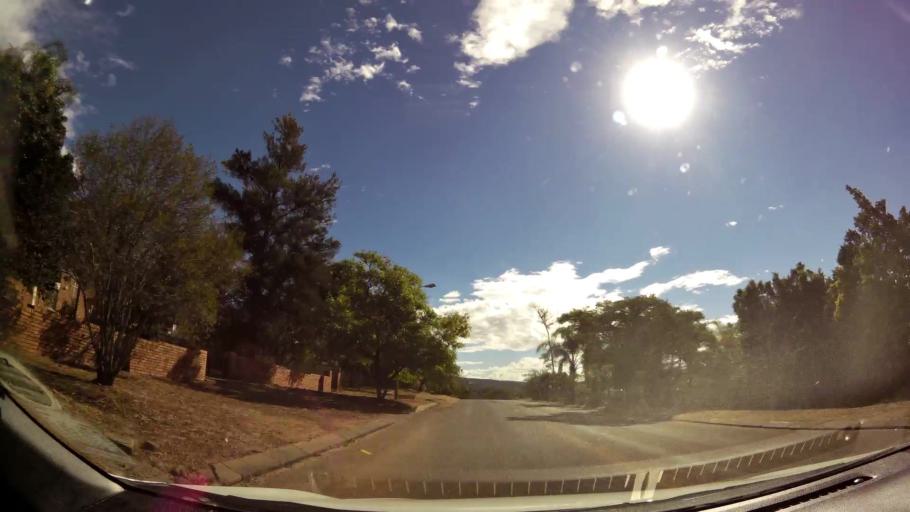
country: ZA
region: Limpopo
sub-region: Waterberg District Municipality
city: Warmbaths
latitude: -24.8716
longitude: 28.2902
